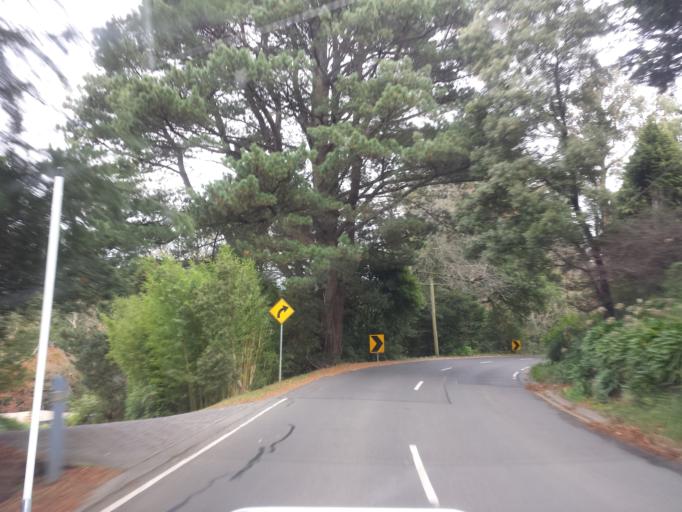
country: AU
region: Victoria
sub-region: Yarra Ranges
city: Monbulk
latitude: -37.8850
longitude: 145.3948
